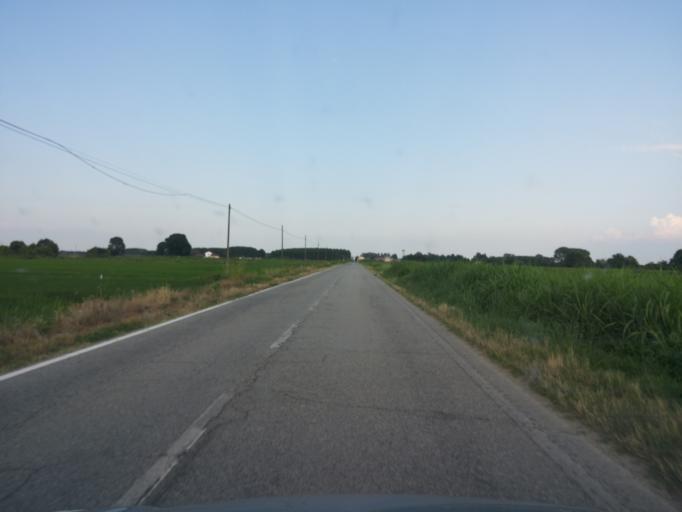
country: IT
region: Piedmont
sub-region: Provincia di Vercelli
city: Asigliano Vercellese
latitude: 45.2646
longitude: 8.3865
